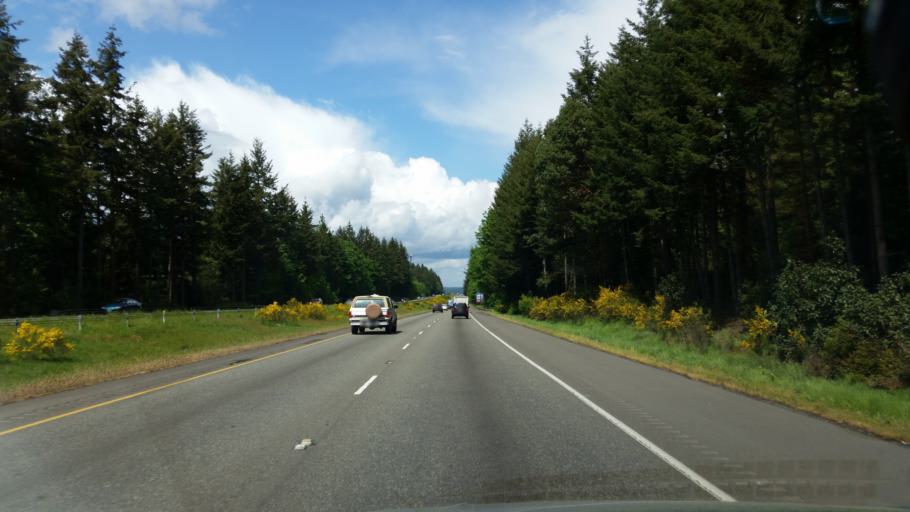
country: US
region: Washington
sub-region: Pierce County
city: Gig Harbor
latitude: 47.3393
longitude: -122.6057
